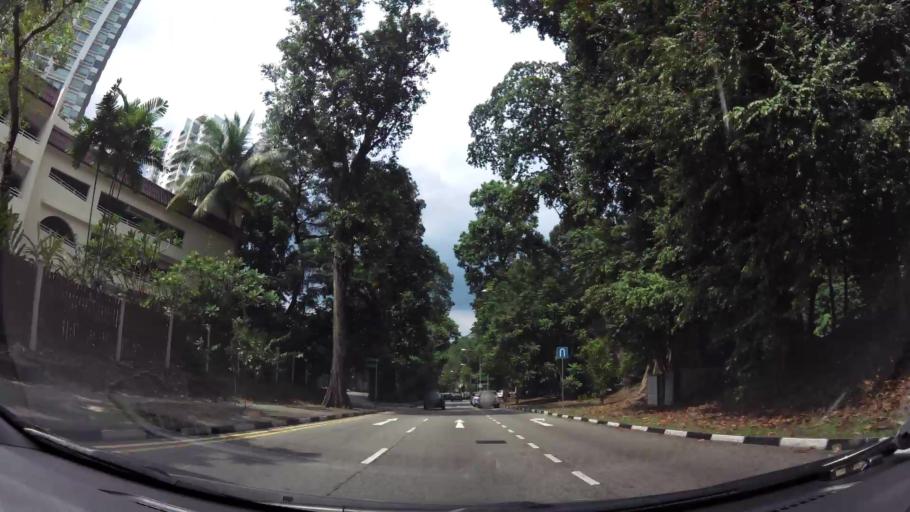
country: SG
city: Singapore
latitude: 1.3102
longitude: 103.8332
